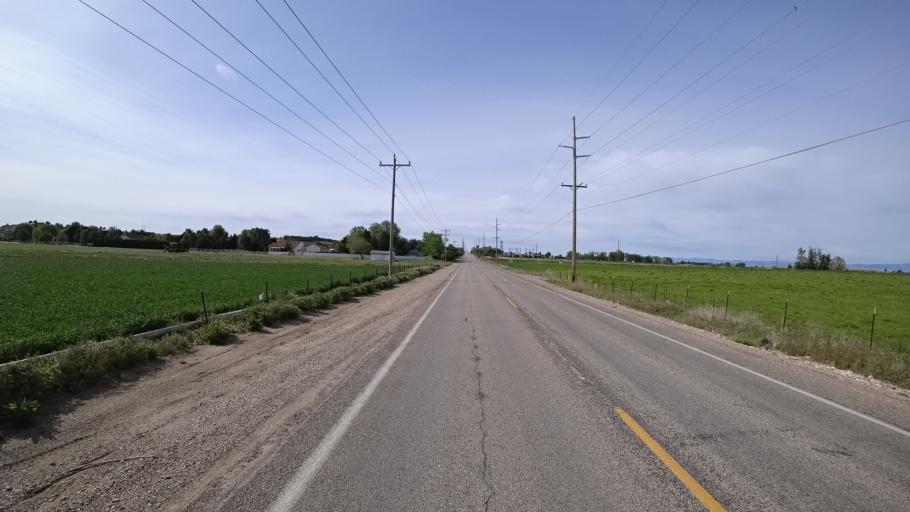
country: US
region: Idaho
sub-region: Ada County
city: Kuna
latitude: 43.5127
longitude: -116.3344
